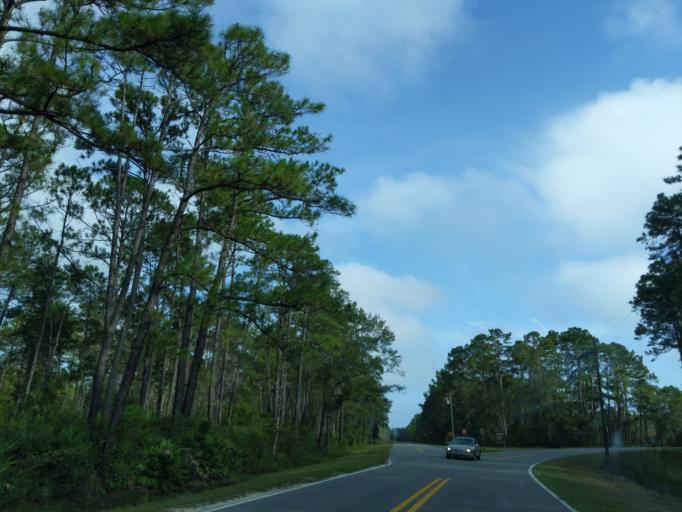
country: US
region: Florida
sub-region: Wakulla County
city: Crawfordville
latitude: 30.1028
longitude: -84.3055
